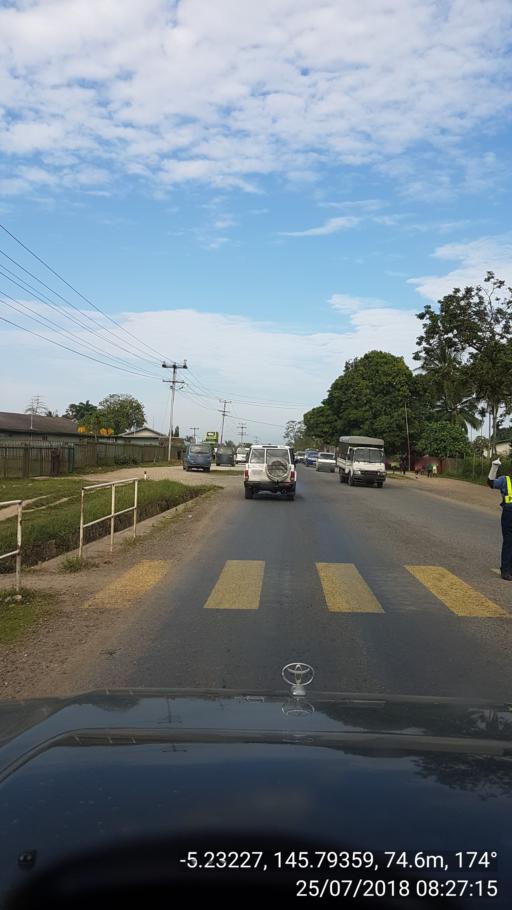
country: PG
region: Madang
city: Madang
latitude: -5.2321
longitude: 145.7934
